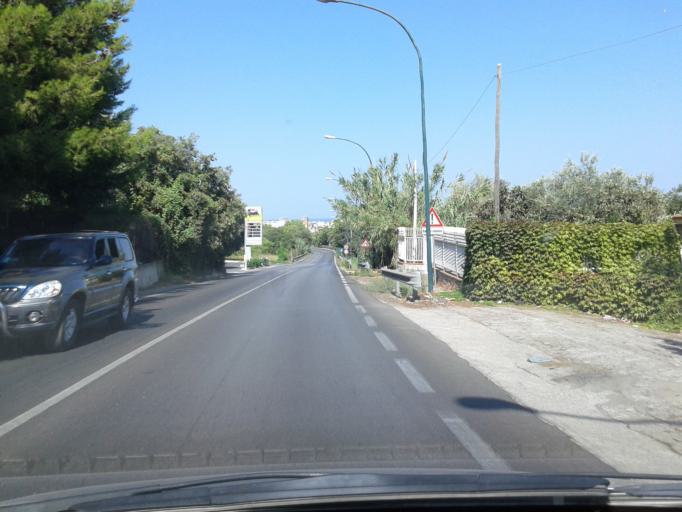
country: IT
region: Sicily
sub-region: Palermo
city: Monreale
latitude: 38.0898
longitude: 13.3041
